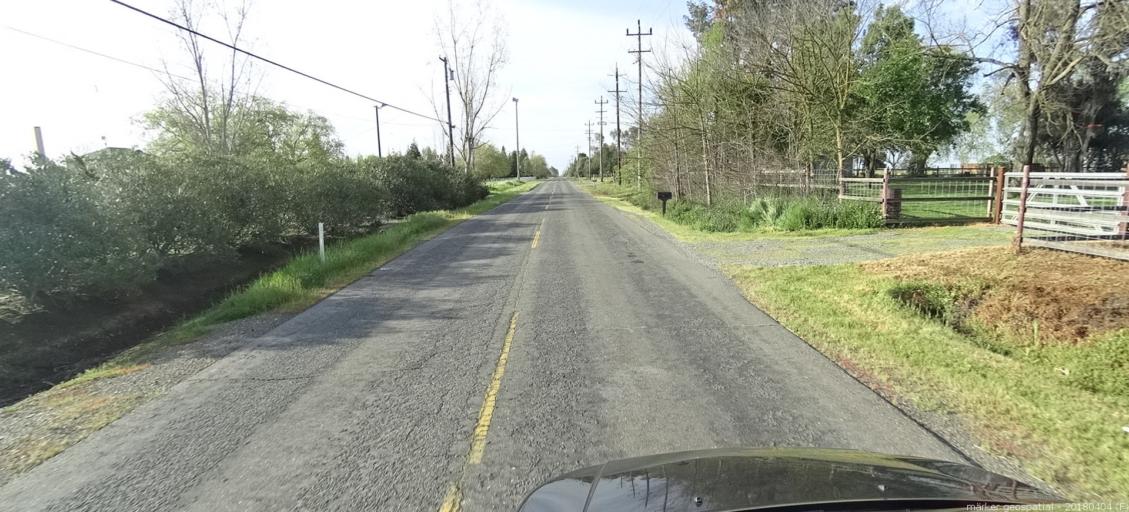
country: US
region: California
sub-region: Sacramento County
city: Herald
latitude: 38.3382
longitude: -121.2421
